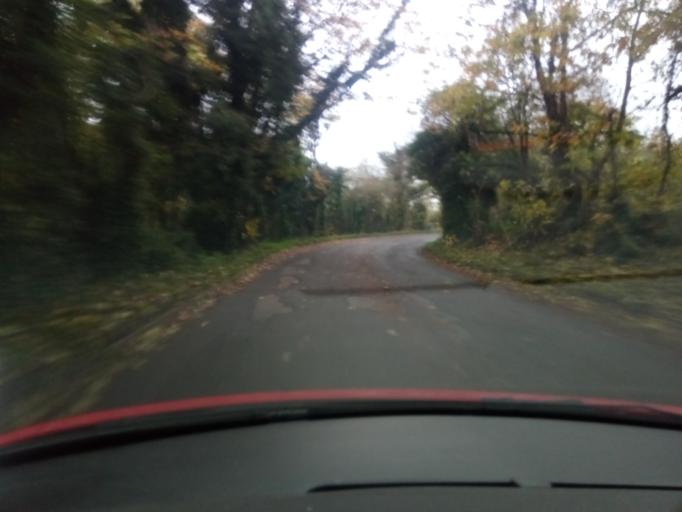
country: GB
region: England
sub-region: Derbyshire
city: Melbourne
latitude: 52.8694
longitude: -1.4283
